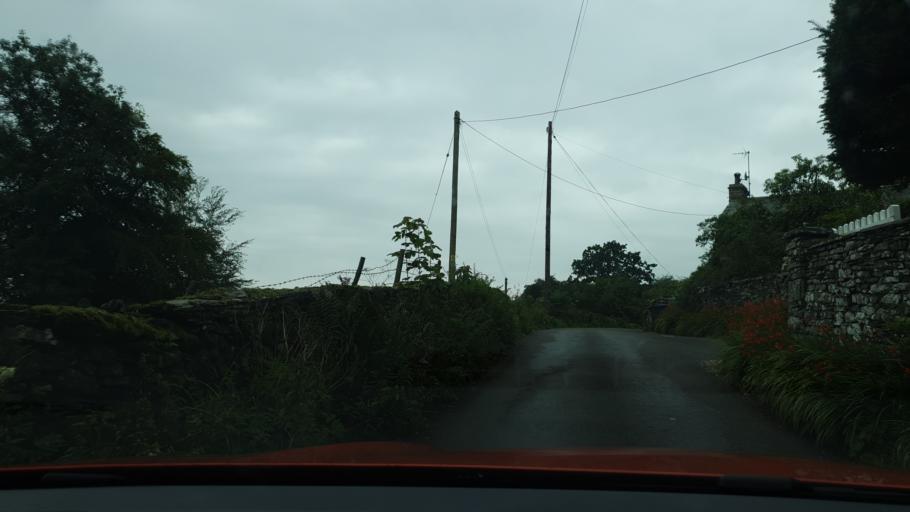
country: GB
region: England
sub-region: Cumbria
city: Grange-over-Sands
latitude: 54.2759
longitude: -2.9826
